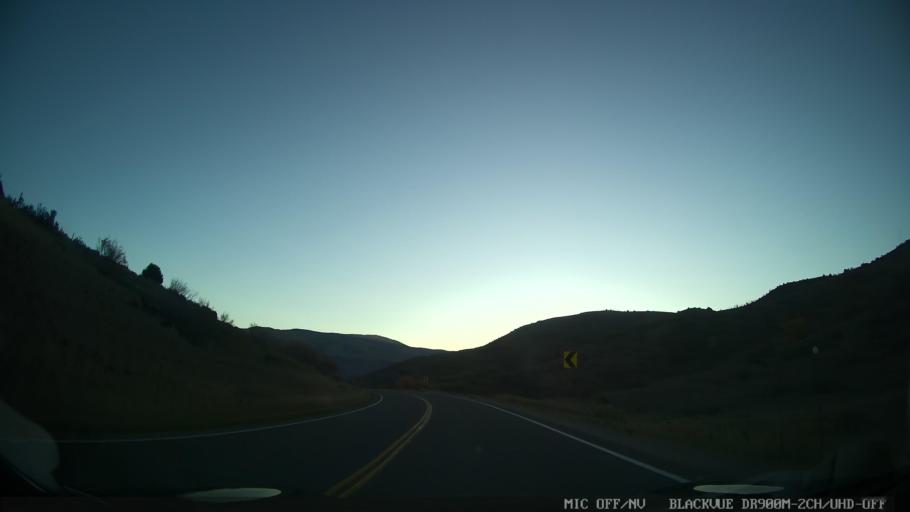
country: US
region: Colorado
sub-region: Eagle County
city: Edwards
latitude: 39.8173
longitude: -106.6543
